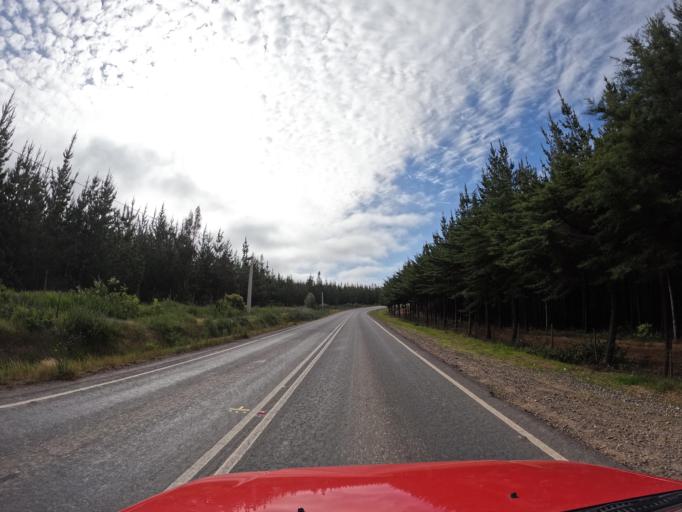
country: CL
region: O'Higgins
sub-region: Provincia de Colchagua
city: Santa Cruz
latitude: -34.3427
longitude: -71.8745
